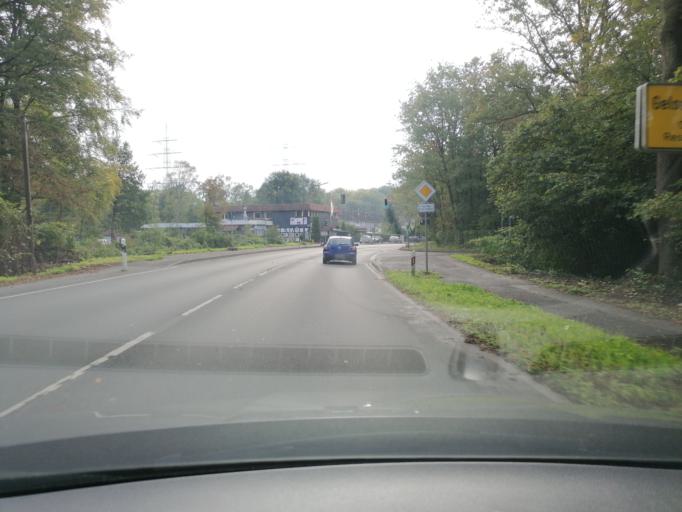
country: DE
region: North Rhine-Westphalia
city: Herten
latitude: 51.5658
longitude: 7.1320
